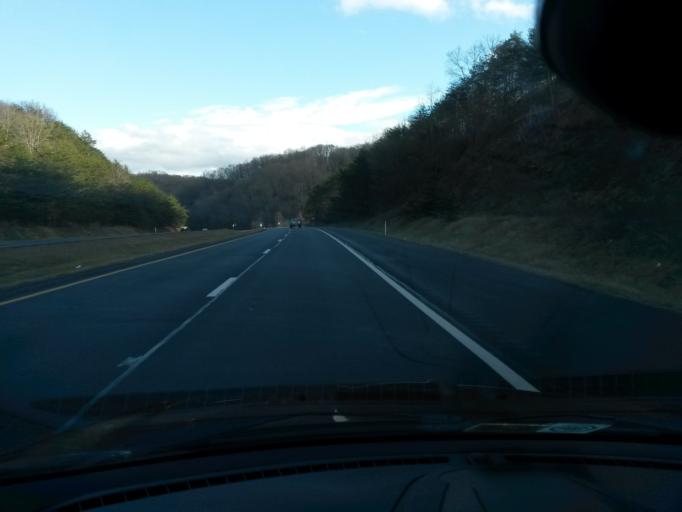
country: US
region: West Virginia
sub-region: Mercer County
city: Athens
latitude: 37.3405
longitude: -80.9760
